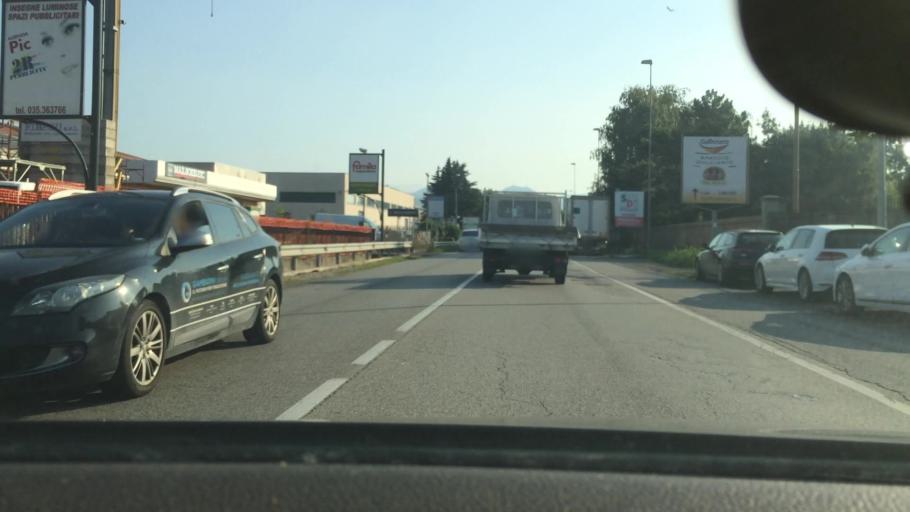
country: IT
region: Lombardy
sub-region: Provincia di Bergamo
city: Lallio
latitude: 45.6588
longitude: 9.6280
